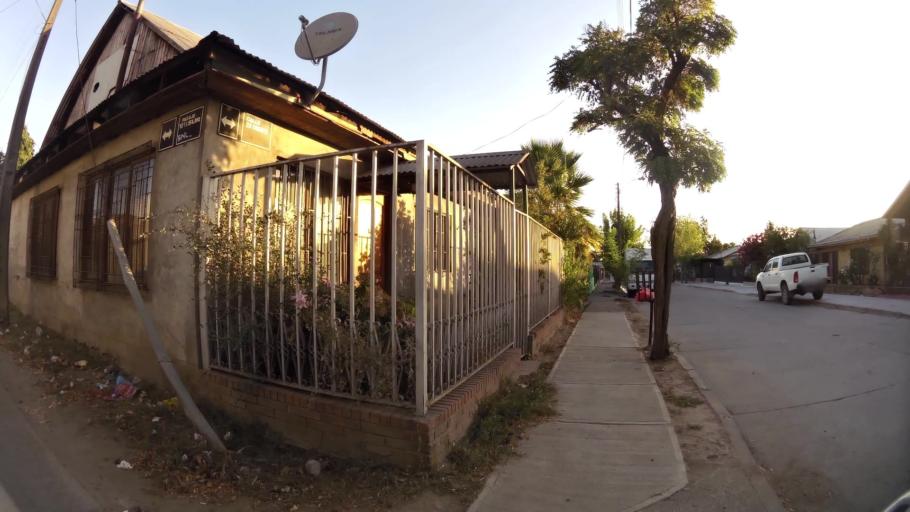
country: CL
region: Maule
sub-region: Provincia de Talca
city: Talca
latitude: -35.4429
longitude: -71.6372
